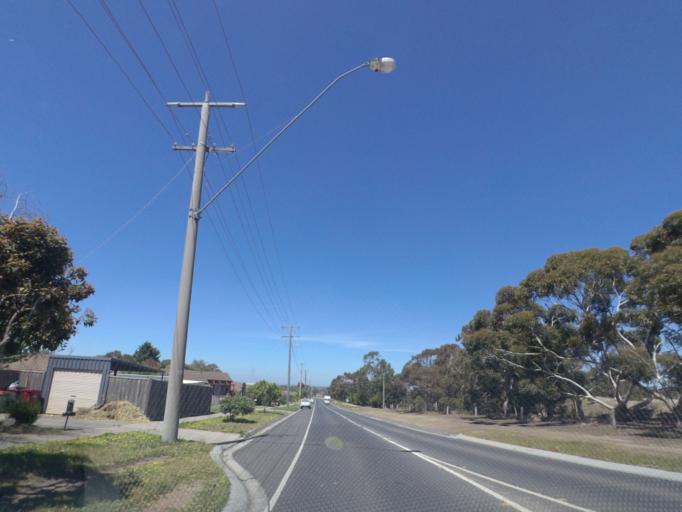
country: AU
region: Victoria
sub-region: Hume
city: Sunbury
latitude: -37.5728
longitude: 144.6944
